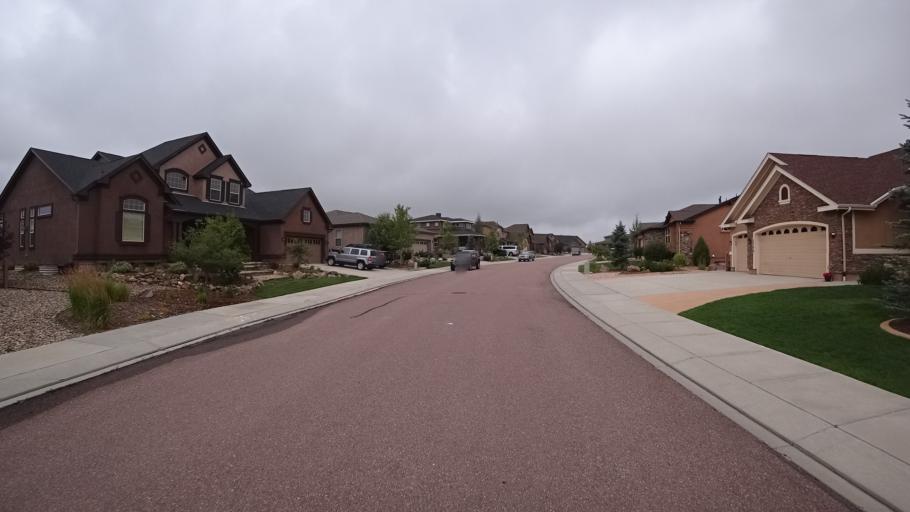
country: US
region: Colorado
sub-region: El Paso County
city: Gleneagle
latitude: 39.0170
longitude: -104.7820
